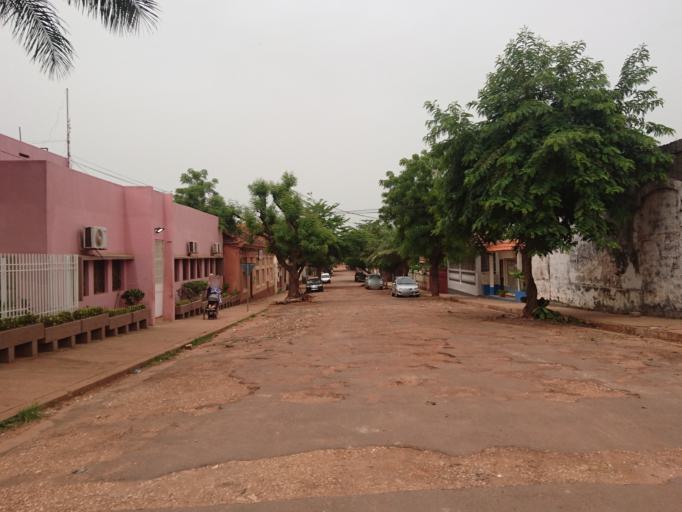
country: GW
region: Bissau
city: Bissau
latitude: 11.8613
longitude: -15.5829
